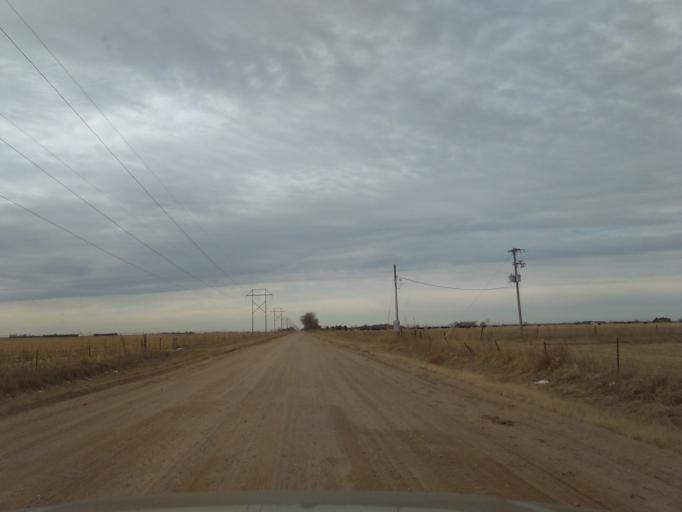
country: US
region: Nebraska
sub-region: Buffalo County
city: Shelton
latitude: 40.6548
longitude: -98.7475
